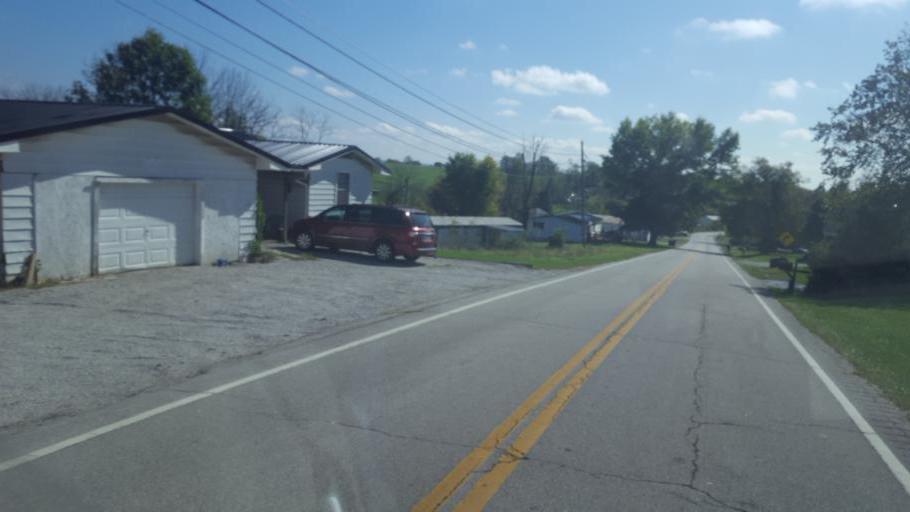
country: US
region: Kentucky
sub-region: Mason County
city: Maysville
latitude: 38.5798
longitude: -83.6486
